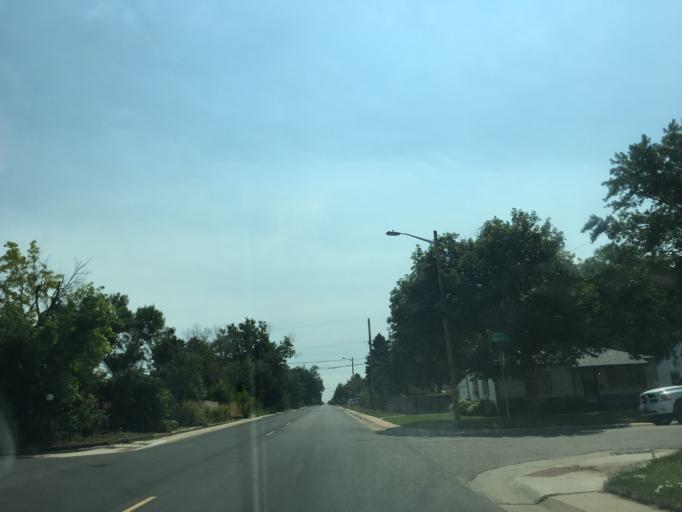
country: US
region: Colorado
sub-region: Jefferson County
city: Lakewood
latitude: 39.6931
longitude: -105.0497
